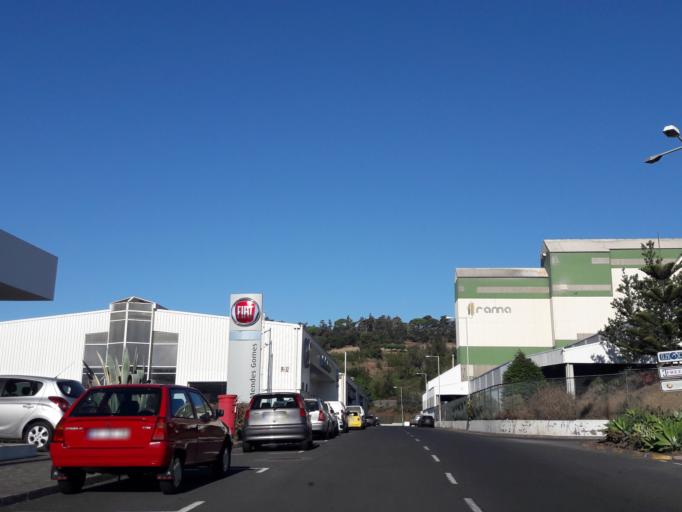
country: PT
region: Madeira
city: Canico
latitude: 32.6519
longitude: -16.8600
